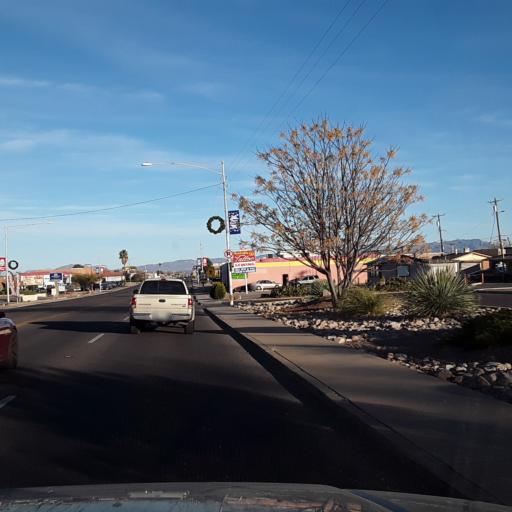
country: US
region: Arizona
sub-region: Cochise County
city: Sierra Vista
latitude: 31.5545
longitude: -110.2997
